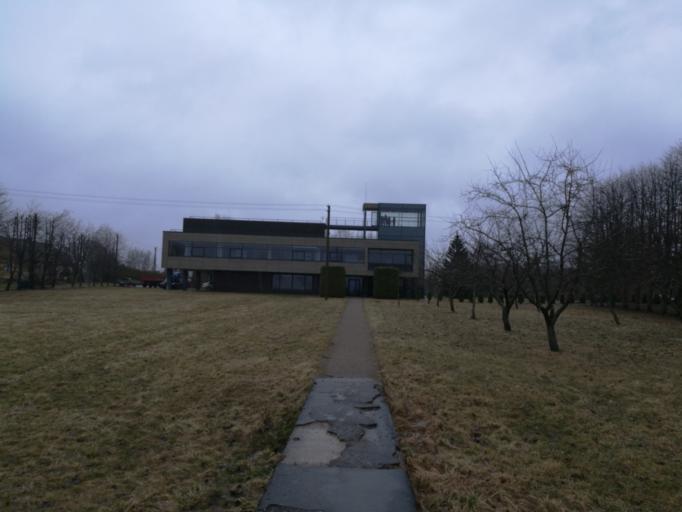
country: LT
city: Simnas
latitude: 54.4572
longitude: 23.6391
